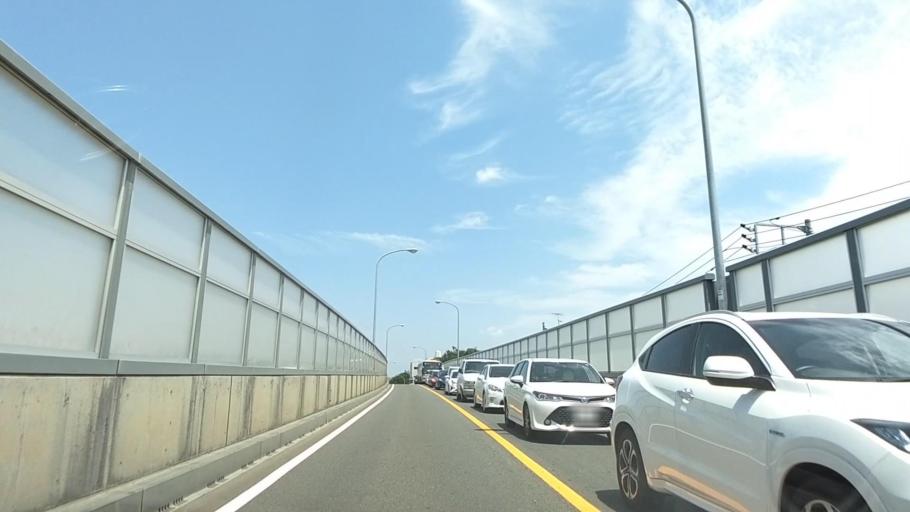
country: JP
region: Kanagawa
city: Minami-rinkan
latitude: 35.4696
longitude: 139.4805
